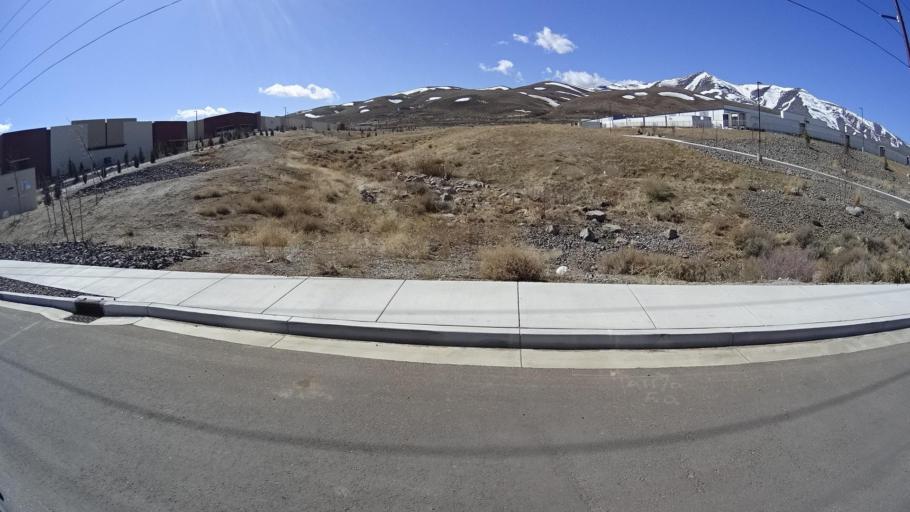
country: US
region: Nevada
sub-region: Washoe County
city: Lemmon Valley
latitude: 39.6060
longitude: -119.8772
